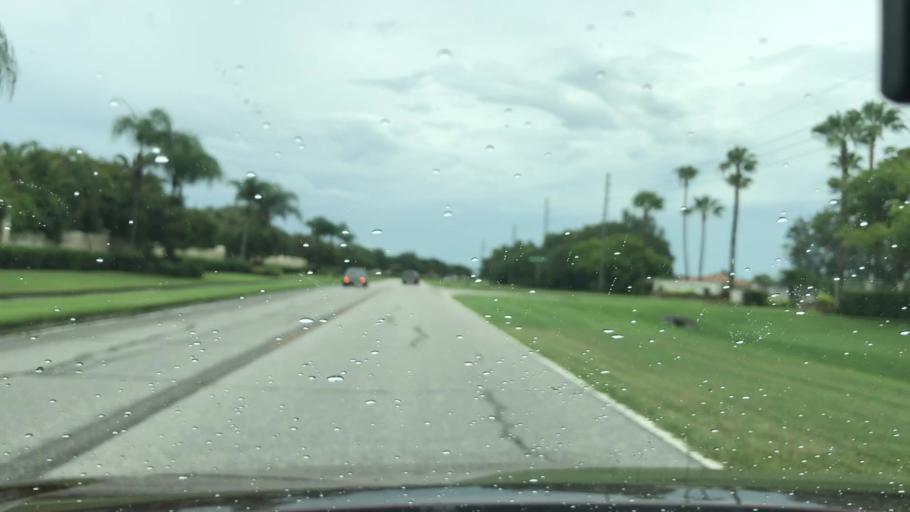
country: US
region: Florida
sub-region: Sarasota County
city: Lake Sarasota
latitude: 27.3076
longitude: -82.3959
